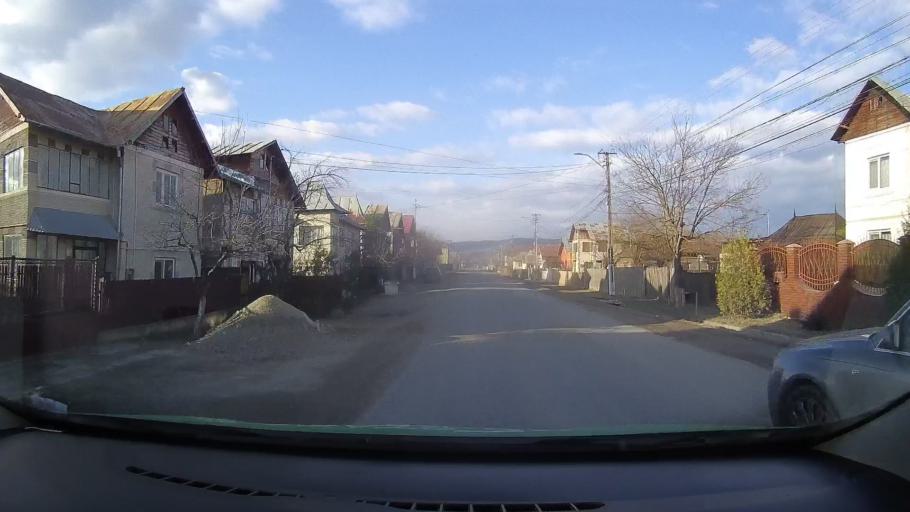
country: RO
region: Dambovita
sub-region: Comuna Ocnita
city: Ocnita
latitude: 44.9740
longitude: 25.5562
